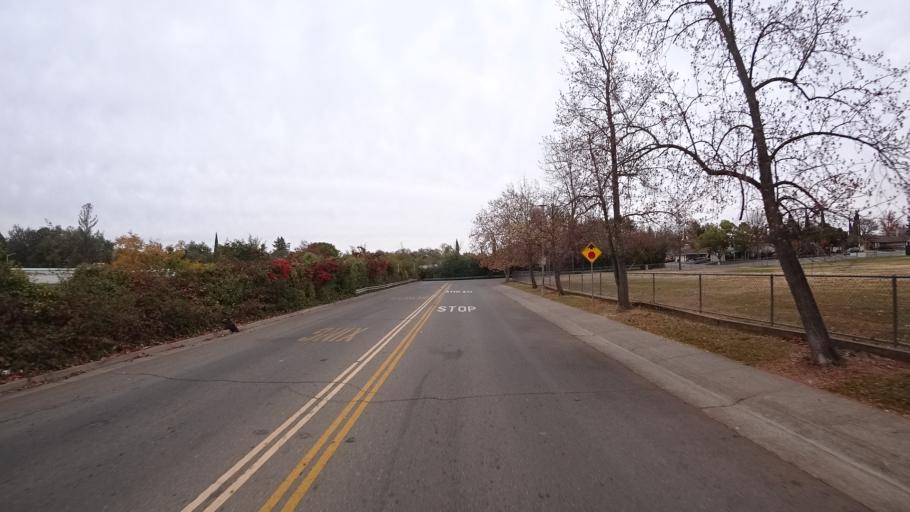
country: US
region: California
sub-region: Sacramento County
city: Citrus Heights
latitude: 38.7037
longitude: -121.2959
